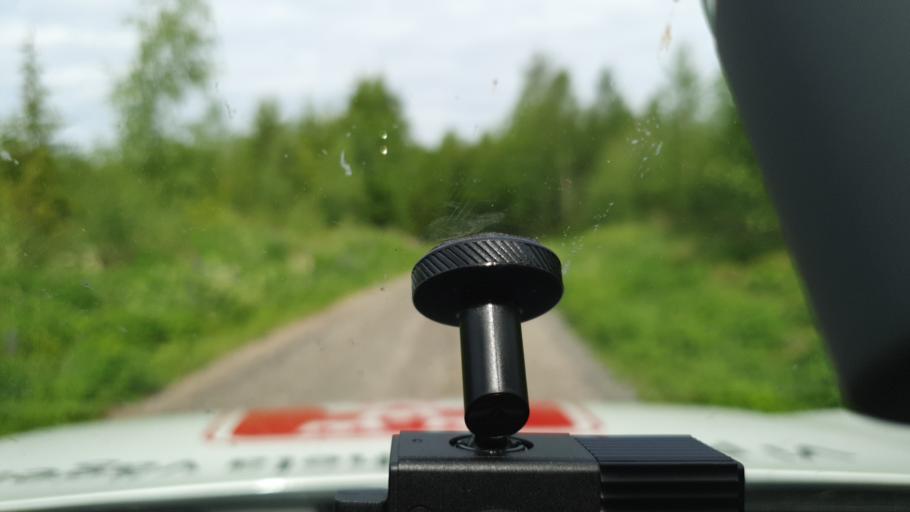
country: SE
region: Vaermland
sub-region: Torsby Kommun
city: Torsby
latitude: 60.2689
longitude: 13.0532
